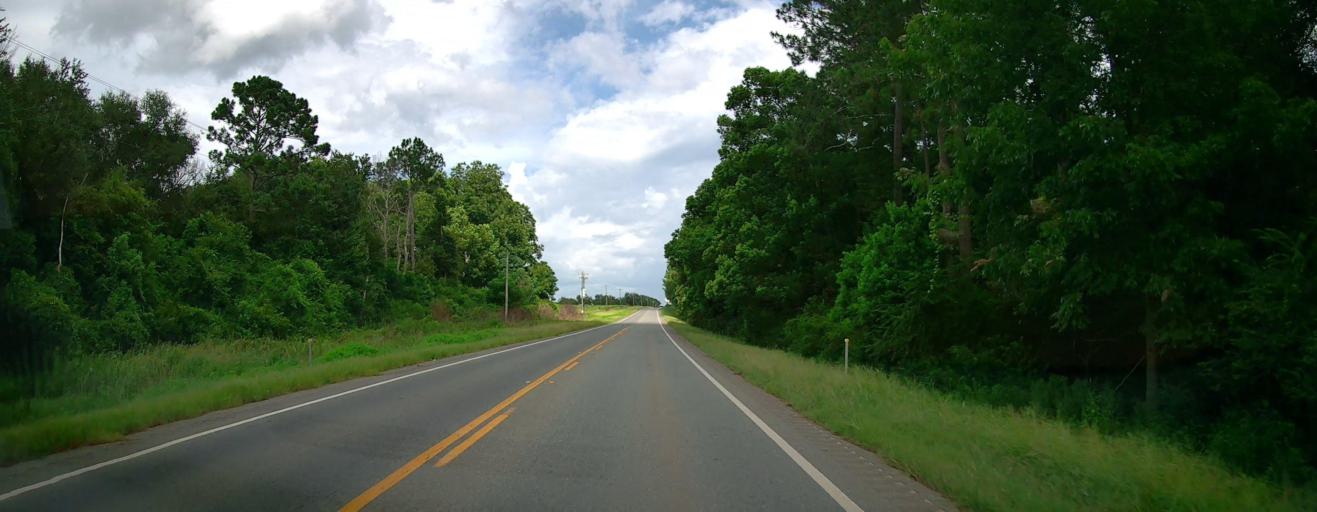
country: US
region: Georgia
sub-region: Coffee County
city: Douglas
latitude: 31.5390
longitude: -82.8795
